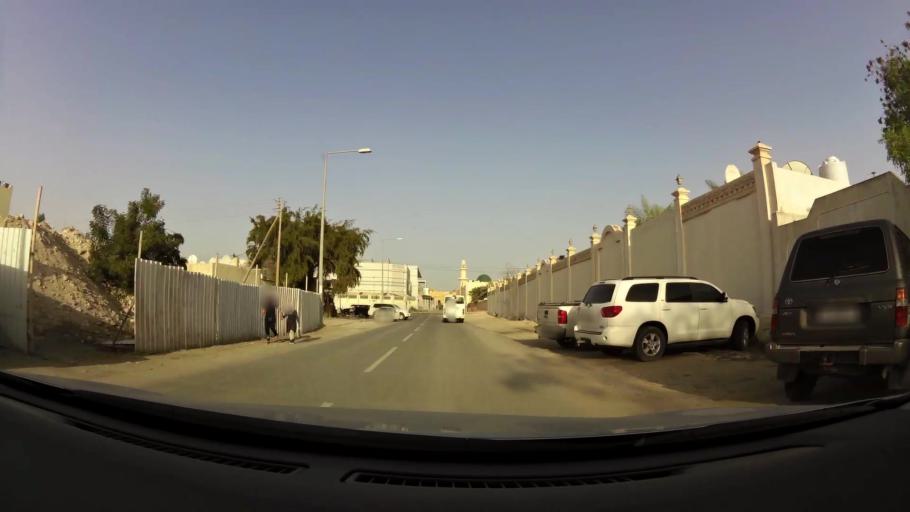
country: QA
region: Baladiyat ar Rayyan
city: Ar Rayyan
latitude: 25.3309
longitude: 51.4544
